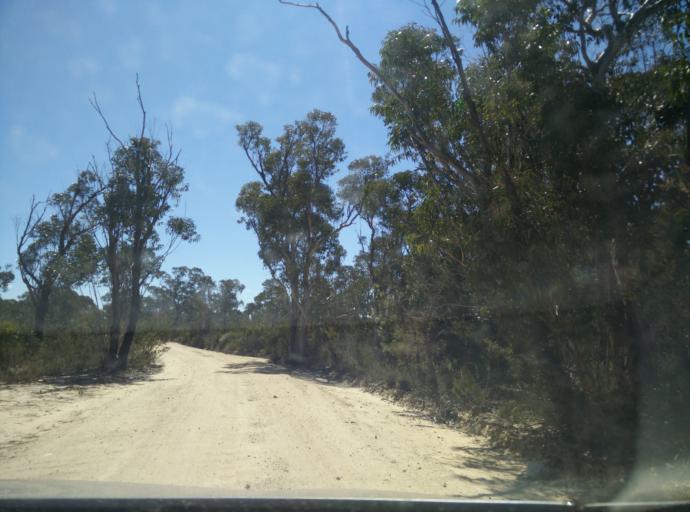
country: AU
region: New South Wales
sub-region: Blue Mountains Municipality
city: Blackheath
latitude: -33.5834
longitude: 150.2744
